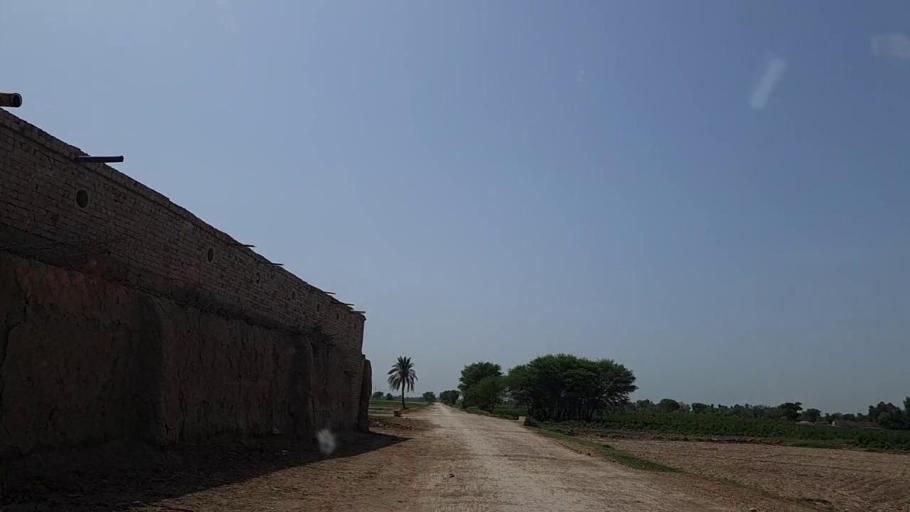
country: PK
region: Sindh
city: Naushahro Firoz
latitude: 26.8495
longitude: 68.0107
